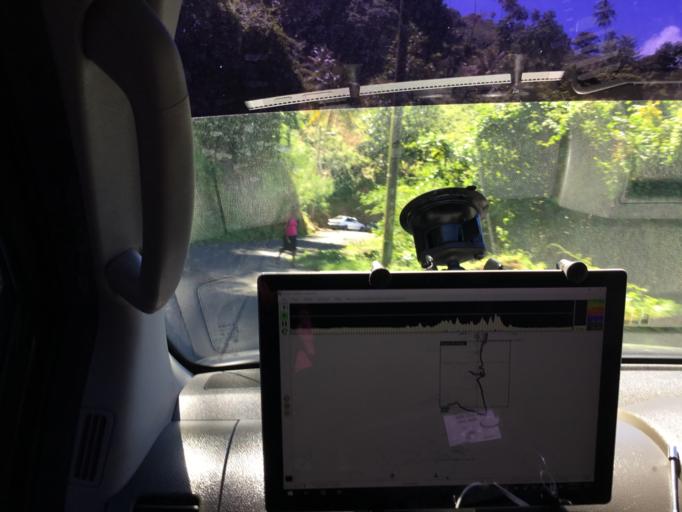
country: VC
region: Charlotte
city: Byera Village
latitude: 13.2445
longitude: -61.1383
